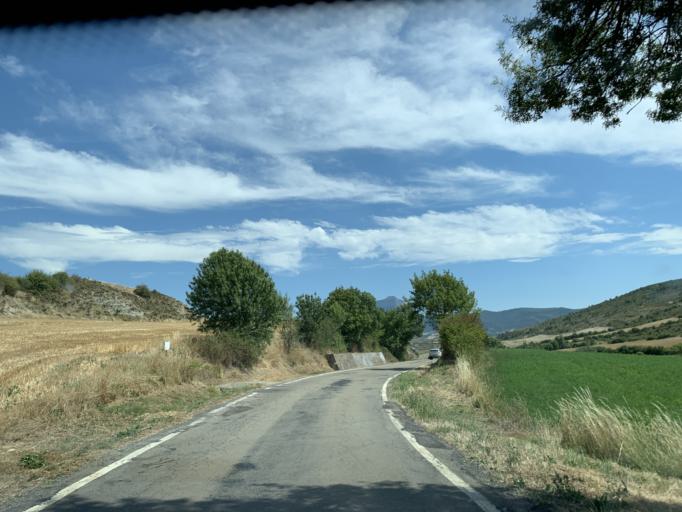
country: ES
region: Aragon
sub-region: Provincia de Huesca
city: Santa Cruz de la Seros
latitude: 42.5946
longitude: -0.6444
